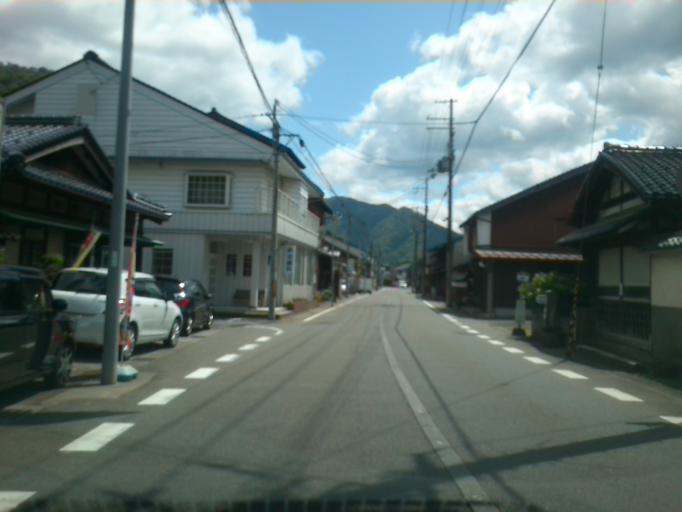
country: JP
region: Hyogo
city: Toyooka
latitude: 35.4639
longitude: 134.8714
